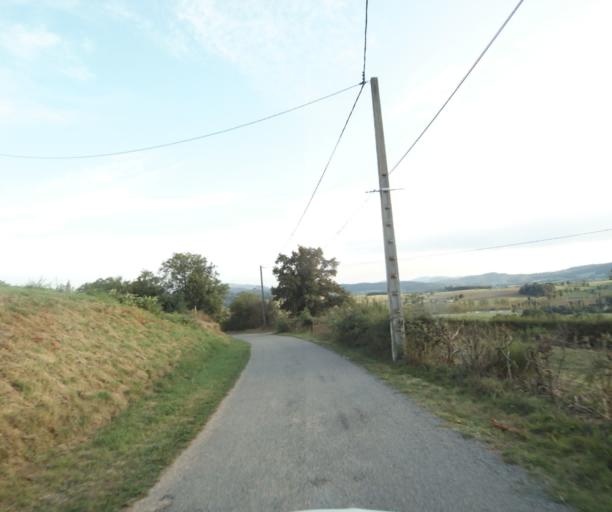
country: FR
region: Bourgogne
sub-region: Departement de Saone-et-Loire
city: Charolles
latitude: 46.3968
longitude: 4.3966
